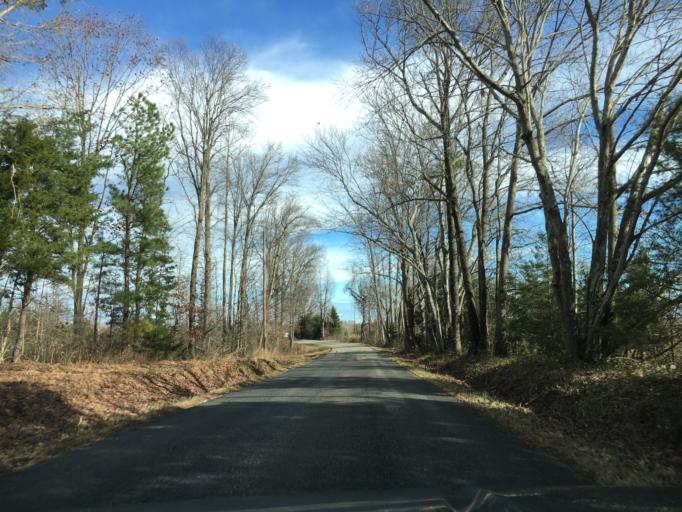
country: US
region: Virginia
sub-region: Nottoway County
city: Crewe
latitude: 37.2679
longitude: -78.2193
